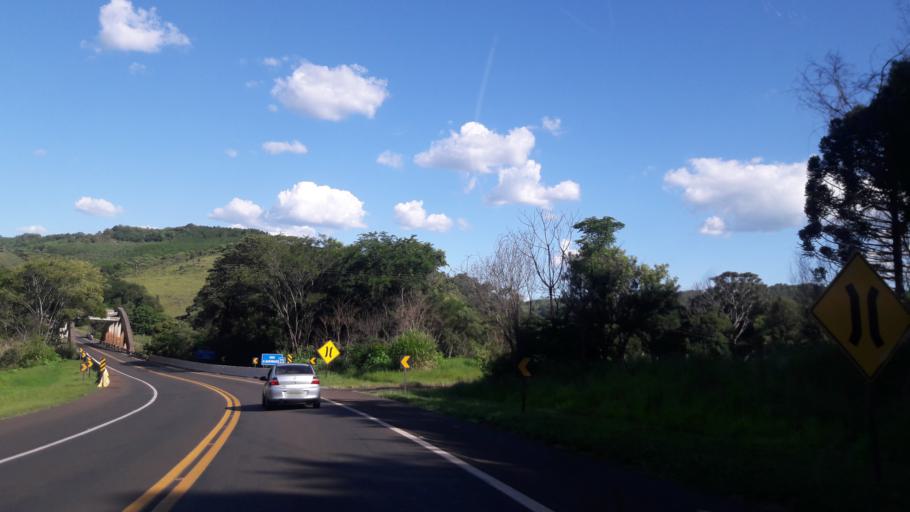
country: BR
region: Parana
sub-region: Laranjeiras Do Sul
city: Laranjeiras do Sul
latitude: -25.4187
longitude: -52.0691
